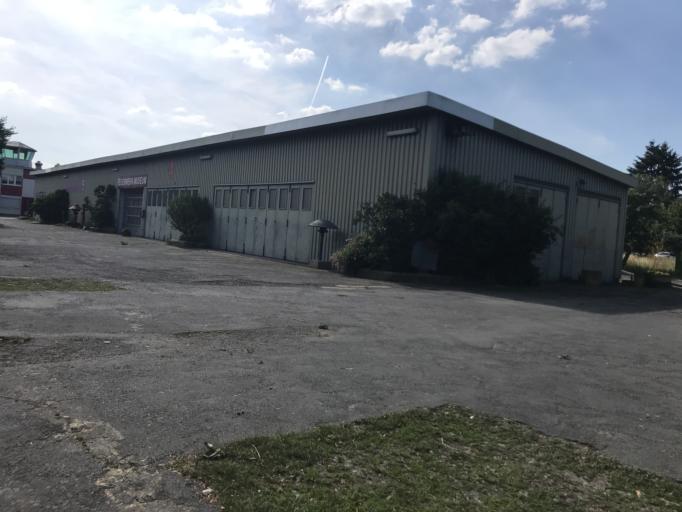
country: DE
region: Hesse
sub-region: Regierungsbezirk Darmstadt
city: Bad Homburg vor der Hoehe
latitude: 50.1780
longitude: 8.6615
